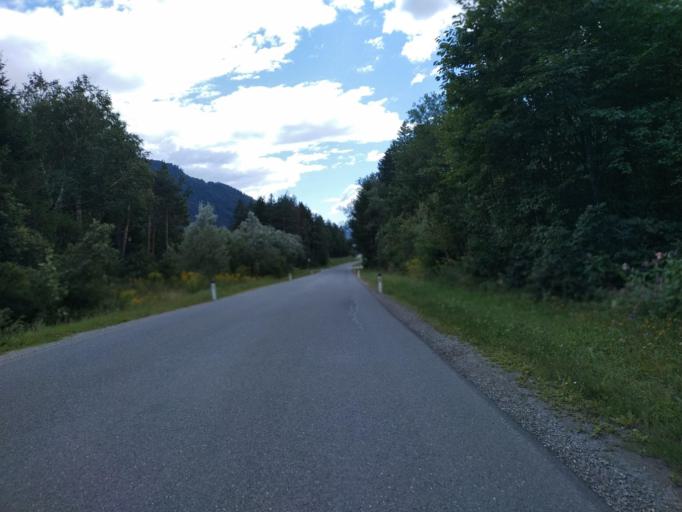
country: AT
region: Tyrol
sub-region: Politischer Bezirk Lienz
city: Schlaiten
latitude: 46.9071
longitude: 12.6201
